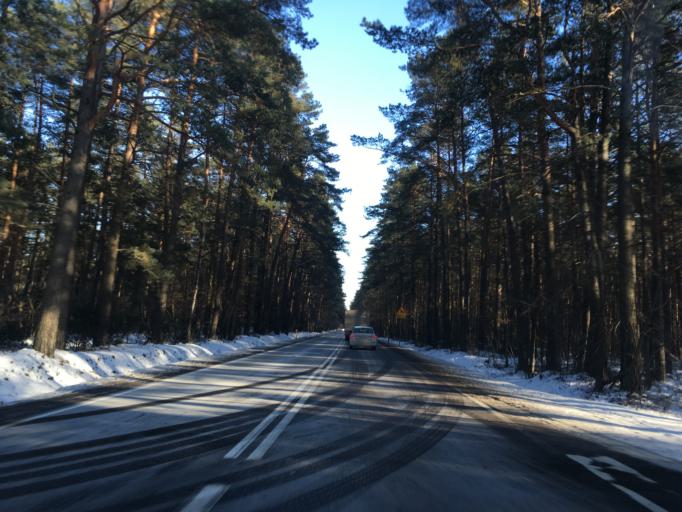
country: PL
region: Pomeranian Voivodeship
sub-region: Powiat koscierski
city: Koscierzyna
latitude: 54.1147
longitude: 17.9007
